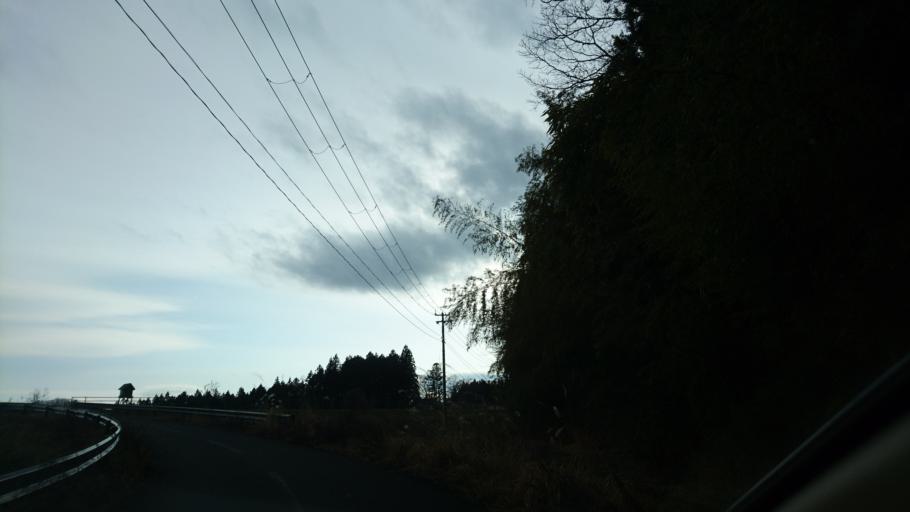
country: JP
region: Iwate
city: Ichinoseki
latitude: 38.9419
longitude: 141.0769
